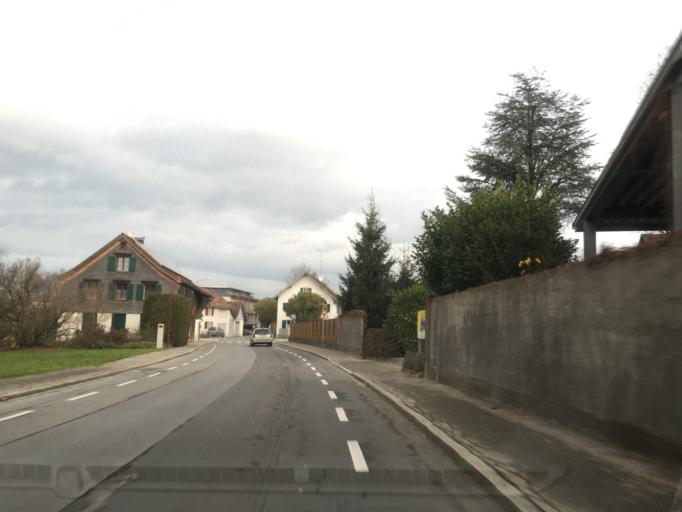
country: AT
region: Vorarlberg
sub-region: Politischer Bezirk Feldkirch
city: Gotzis
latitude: 47.3364
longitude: 9.6395
